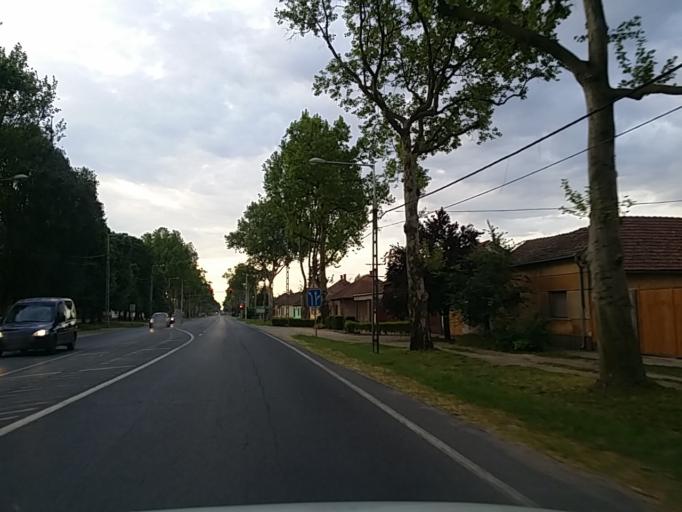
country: HU
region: Bacs-Kiskun
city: Lajosmizse
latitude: 47.0332
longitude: 19.5478
